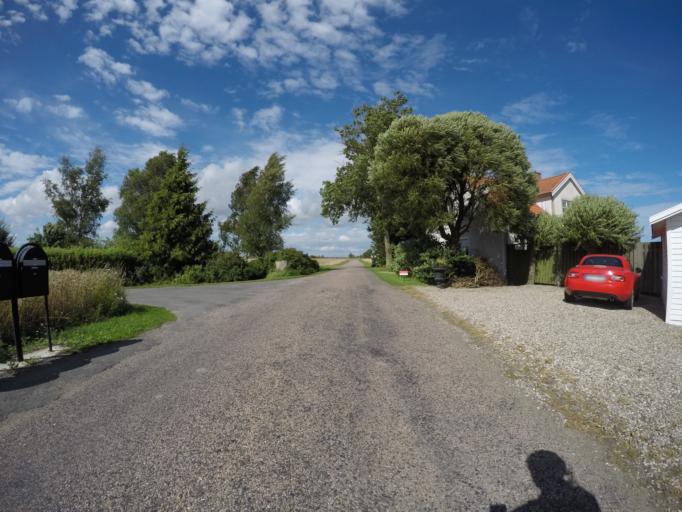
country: SE
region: Skane
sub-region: Simrishamns Kommun
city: Simrishamn
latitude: 55.4816
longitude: 14.1667
